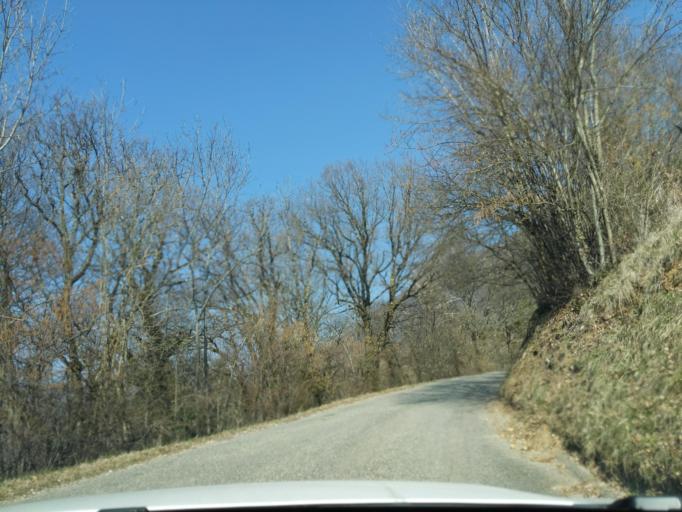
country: FR
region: Rhone-Alpes
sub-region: Departement de la Haute-Savoie
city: Moye
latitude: 45.8915
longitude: 5.8489
